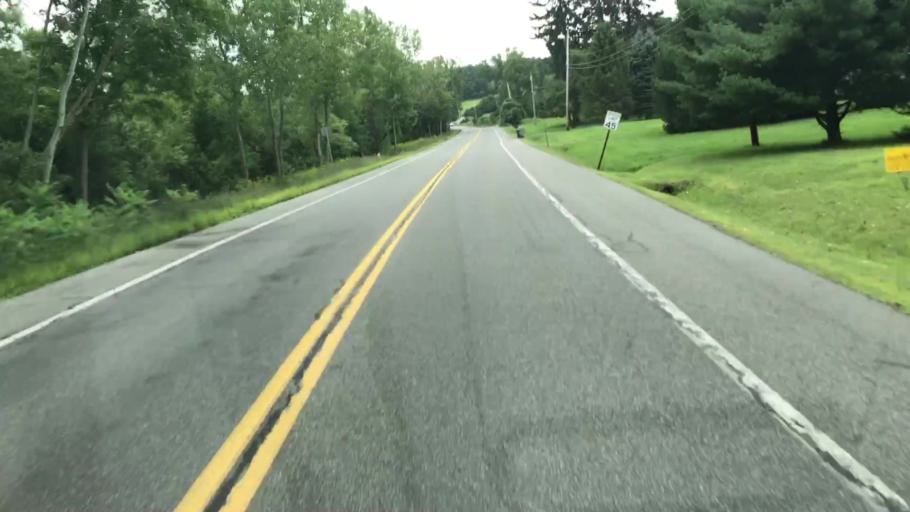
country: US
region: New York
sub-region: Onondaga County
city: Camillus
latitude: 43.0678
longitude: -76.3235
